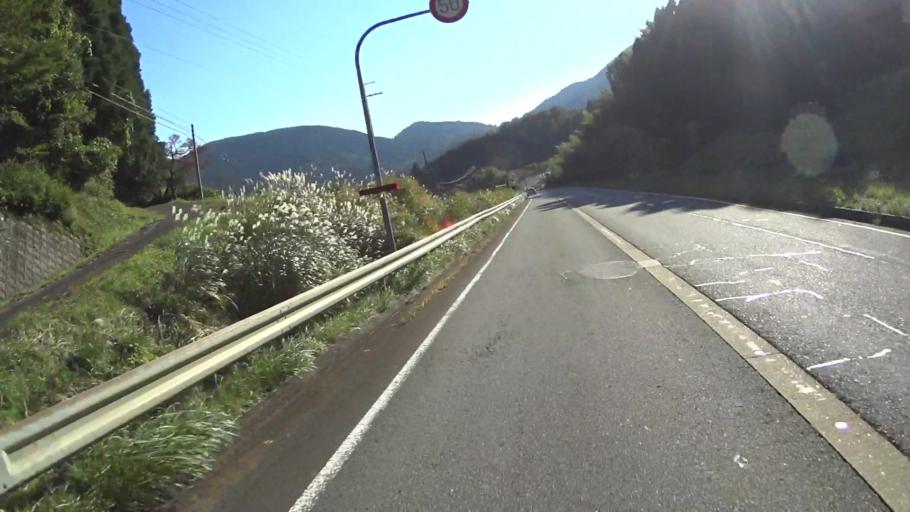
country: JP
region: Kyoto
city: Fukuchiyama
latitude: 35.4073
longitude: 135.0833
